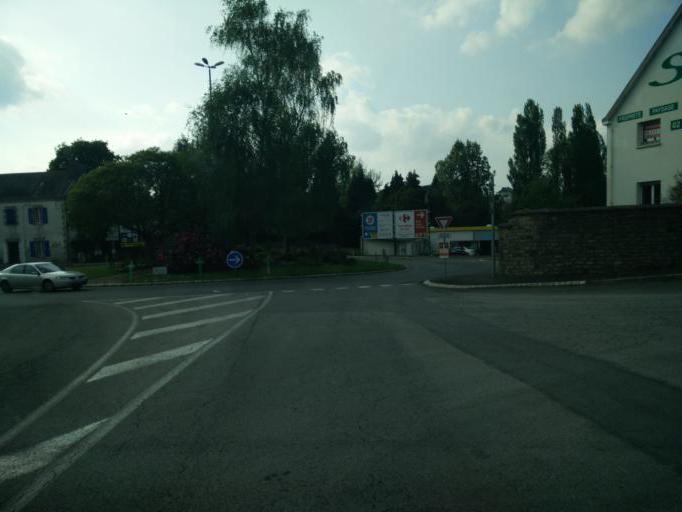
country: FR
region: Brittany
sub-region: Departement du Finistere
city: Quimperle
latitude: 47.8655
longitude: -3.5554
